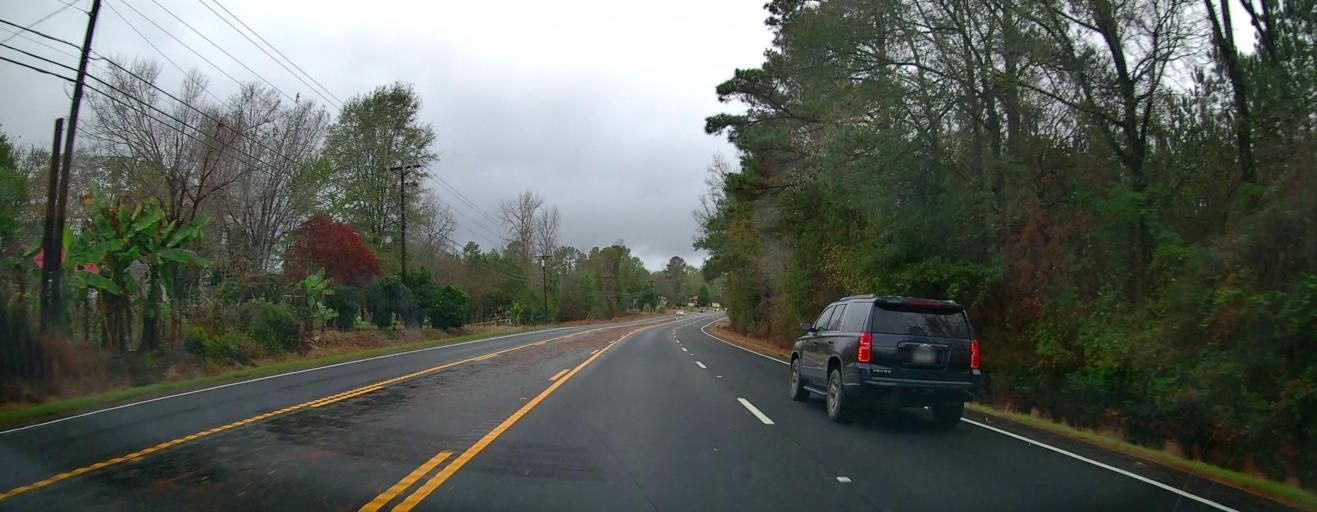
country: US
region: Georgia
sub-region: Clarke County
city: Country Club Estates
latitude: 34.0044
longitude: -83.3861
